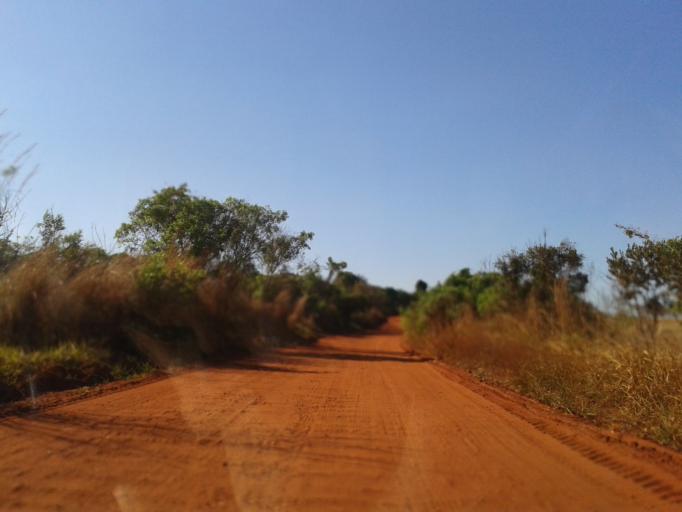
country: BR
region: Minas Gerais
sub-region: Ituiutaba
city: Ituiutaba
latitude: -18.9978
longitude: -49.3715
